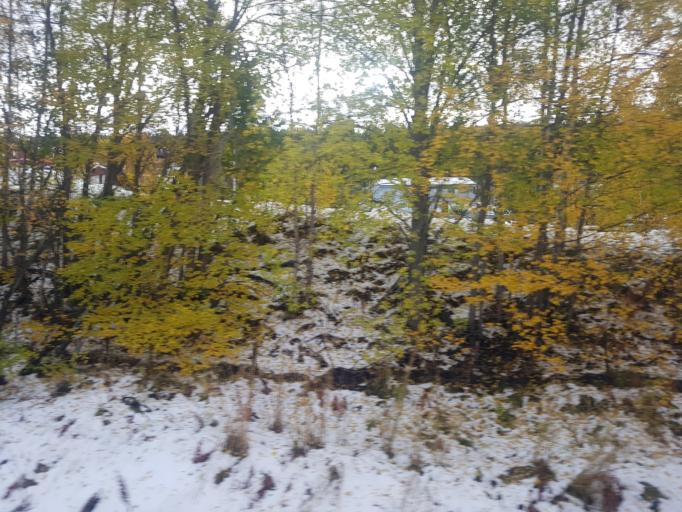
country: NO
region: Oppland
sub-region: Dovre
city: Dombas
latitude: 62.0757
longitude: 9.1287
